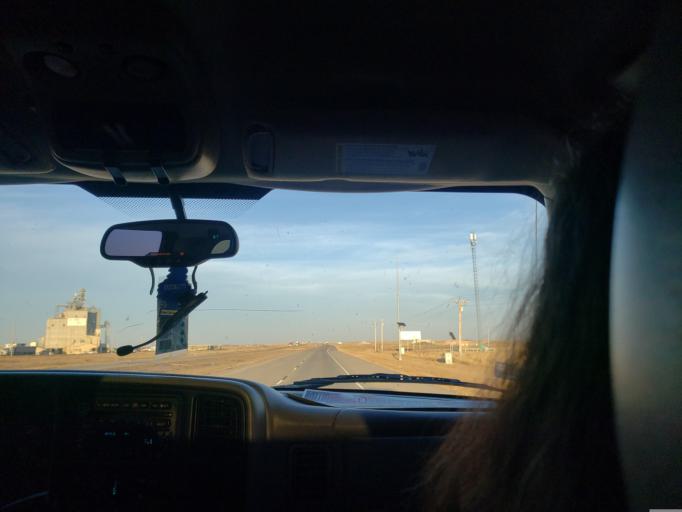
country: US
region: Oklahoma
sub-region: Texas County
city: Guymon
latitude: 36.7678
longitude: -101.3452
